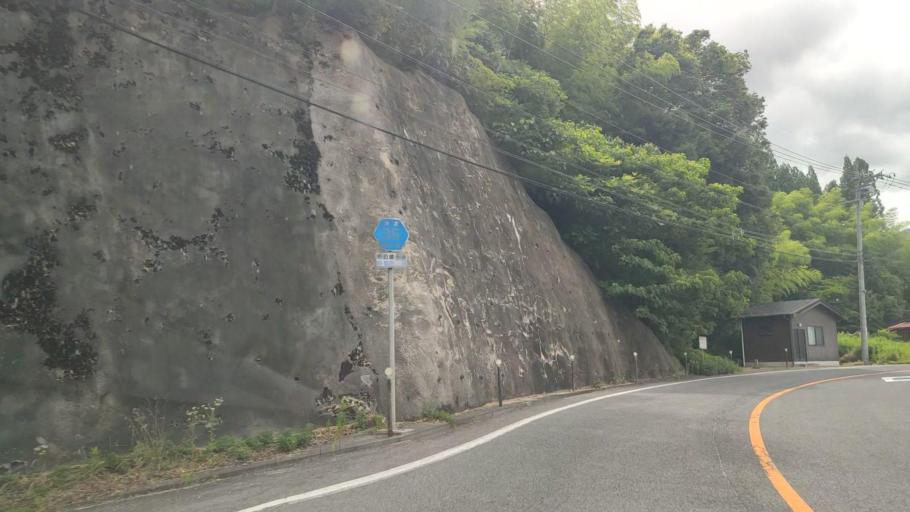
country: JP
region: Tottori
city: Yonago
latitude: 35.2974
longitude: 133.4143
